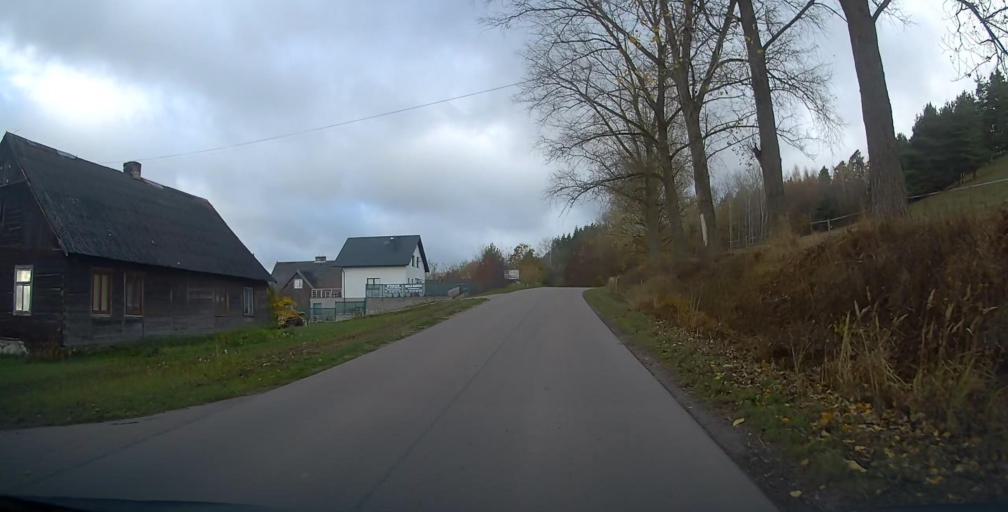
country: PL
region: Podlasie
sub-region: Suwalki
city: Suwalki
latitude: 54.2843
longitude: 22.8956
